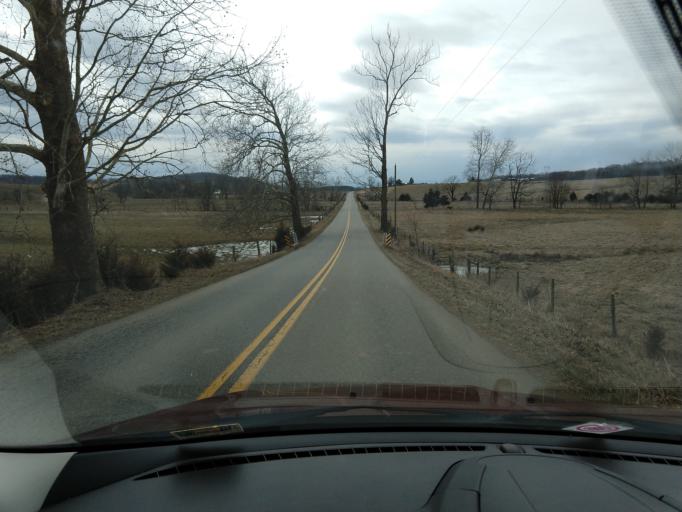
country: US
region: Virginia
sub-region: Augusta County
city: Fishersville
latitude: 38.1578
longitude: -78.9254
